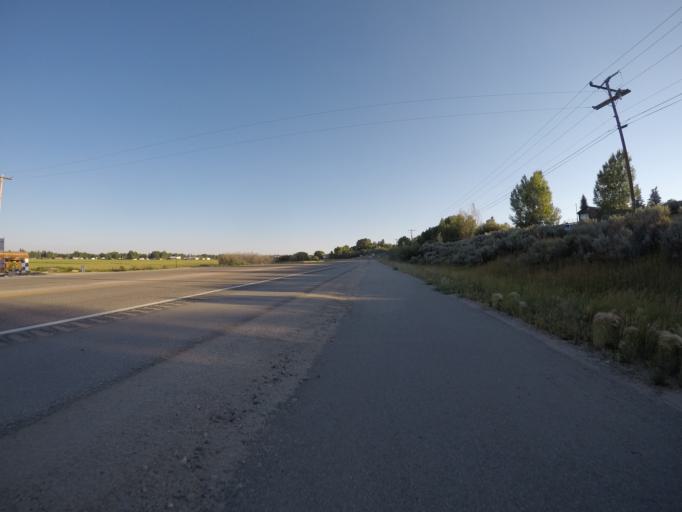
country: US
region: Wyoming
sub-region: Sublette County
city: Pinedale
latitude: 42.8585
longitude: -109.8506
